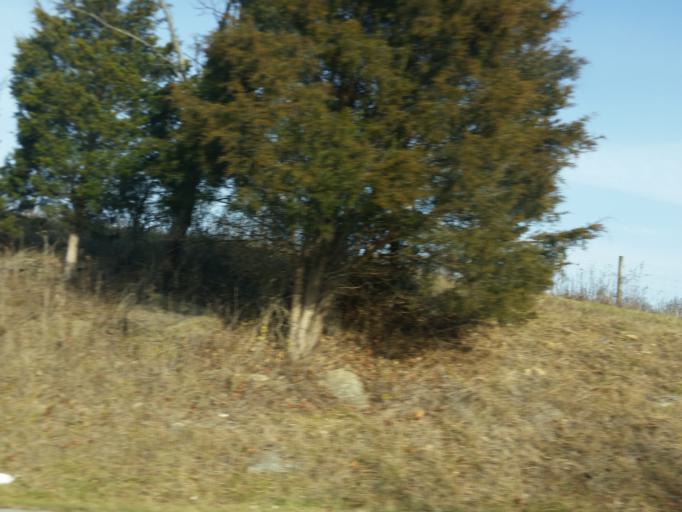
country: US
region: Kentucky
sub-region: Harrison County
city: Cynthiana
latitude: 38.4951
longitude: -84.2858
